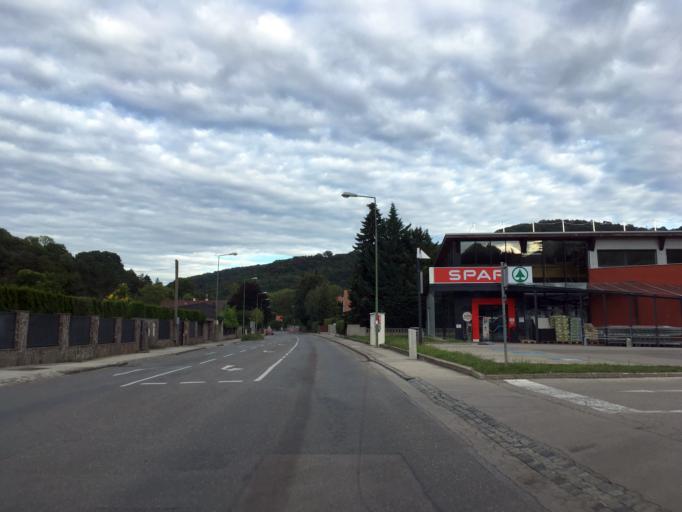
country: AT
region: Lower Austria
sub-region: Politischer Bezirk Wien-Umgebung
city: Klosterneuburg
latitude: 48.3065
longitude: 16.2882
